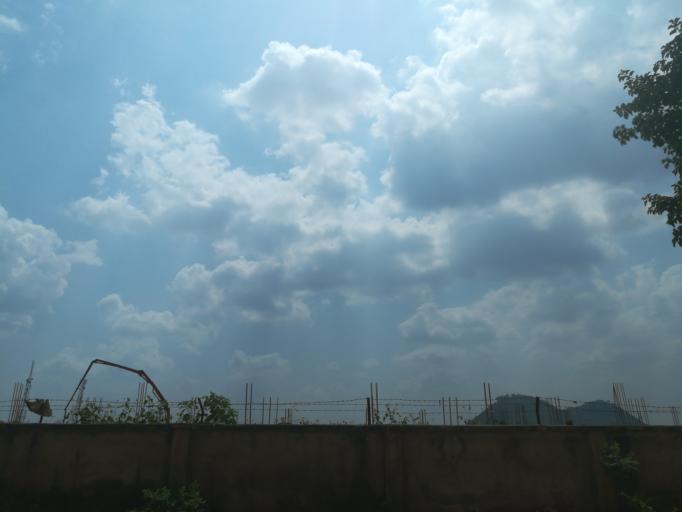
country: NG
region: Abuja Federal Capital Territory
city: Abuja
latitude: 9.0574
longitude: 7.4494
